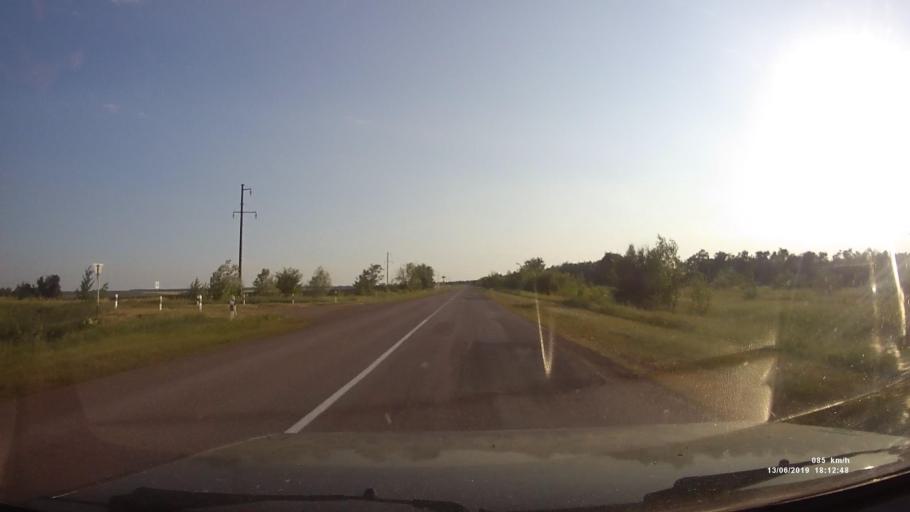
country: RU
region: Rostov
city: Kazanskaya
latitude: 49.9431
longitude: 41.4049
